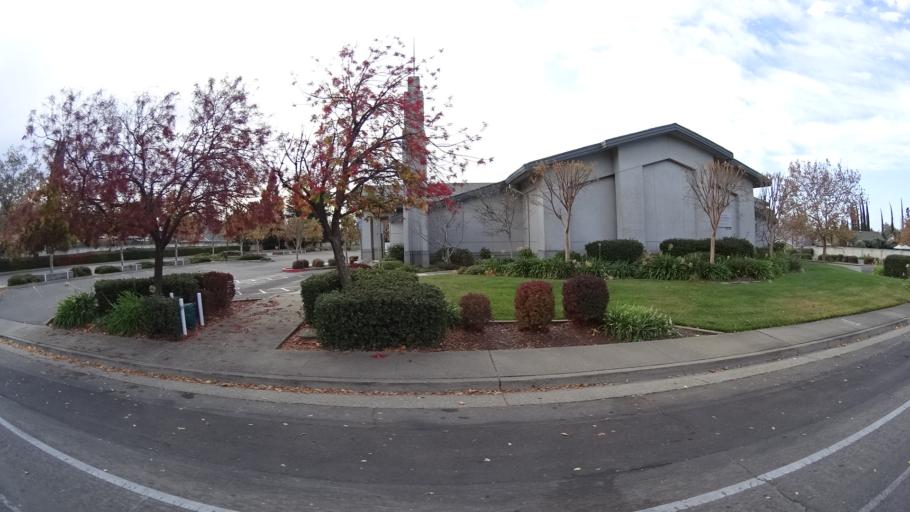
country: US
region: California
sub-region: Sacramento County
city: Citrus Heights
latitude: 38.7004
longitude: -121.2644
